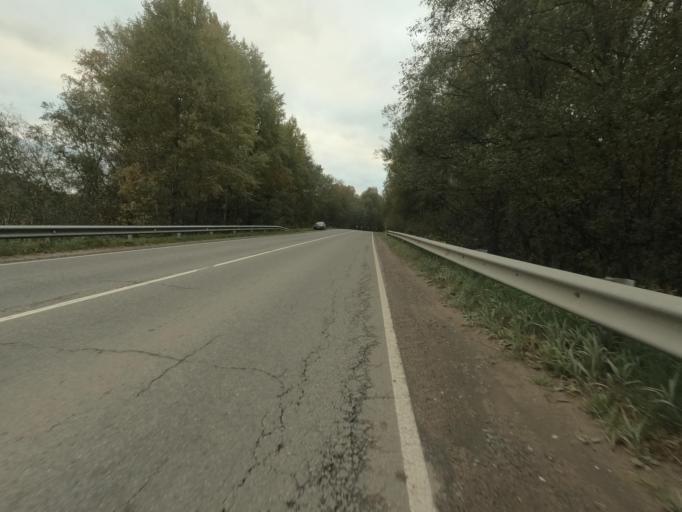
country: RU
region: Leningrad
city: Pavlovo
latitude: 59.7963
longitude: 30.9481
